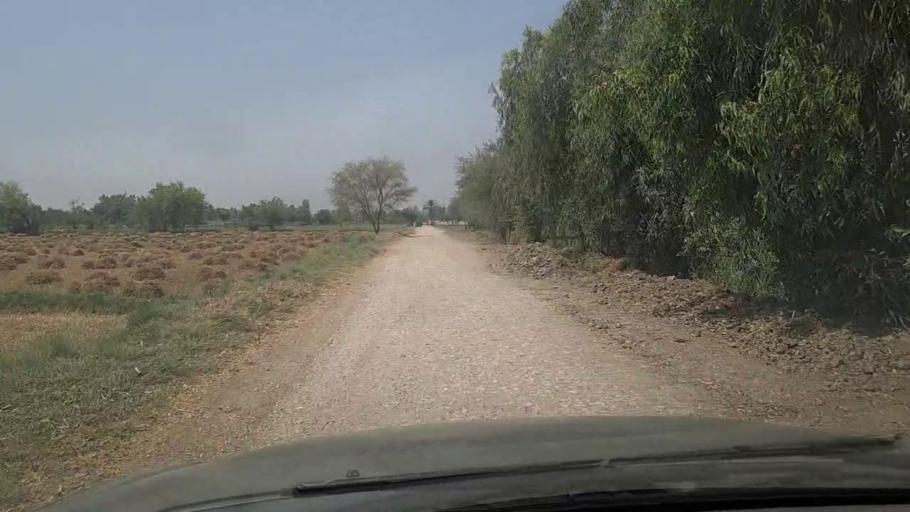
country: PK
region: Sindh
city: Adilpur
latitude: 27.9344
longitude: 69.2726
